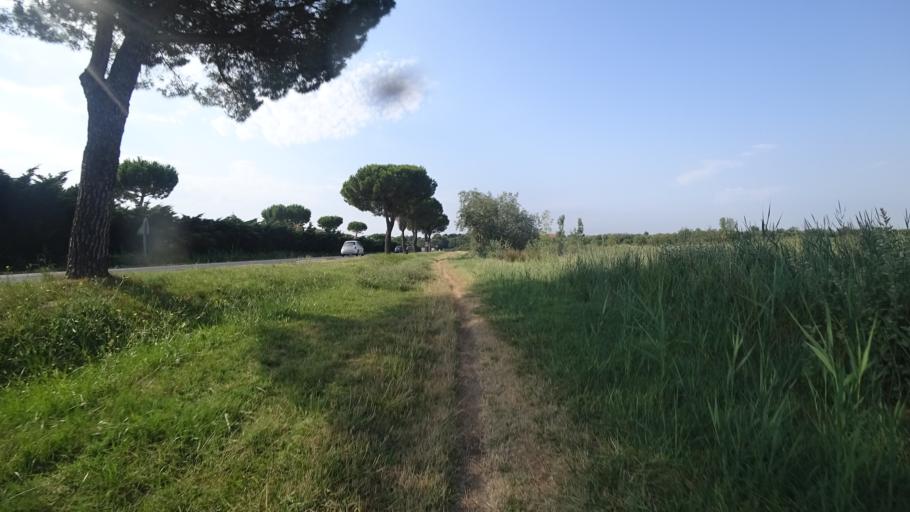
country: FR
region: Languedoc-Roussillon
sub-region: Departement des Pyrenees-Orientales
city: Canet-en-Roussillon
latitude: 42.6937
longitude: 3.0254
